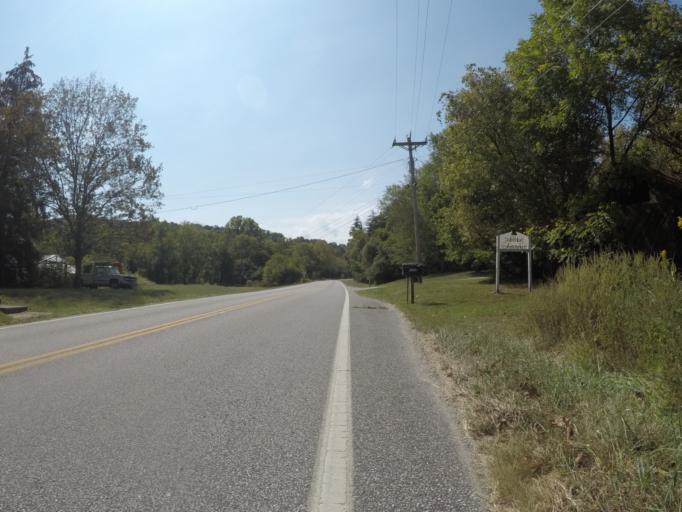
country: US
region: West Virginia
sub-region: Cabell County
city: Lesage
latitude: 38.5202
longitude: -82.3882
